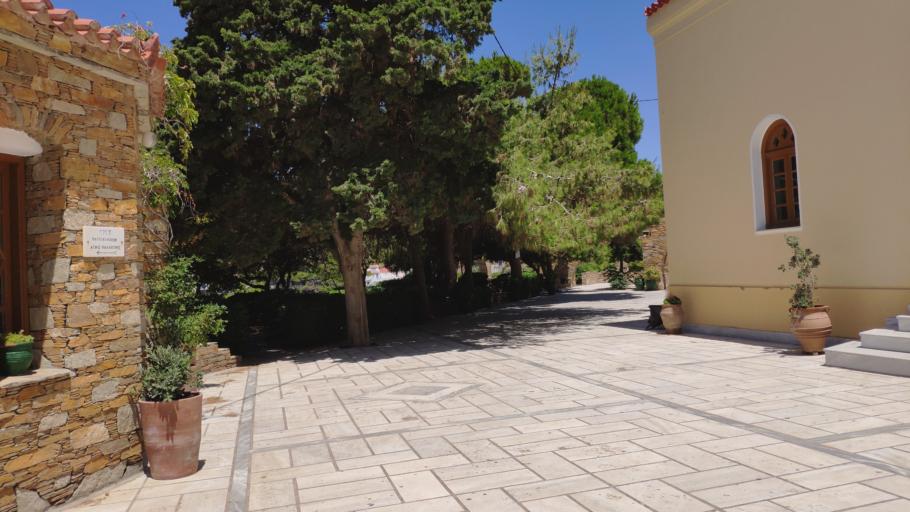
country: GR
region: South Aegean
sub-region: Nomos Kykladon
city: Kythnos
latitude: 37.3446
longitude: 24.4361
